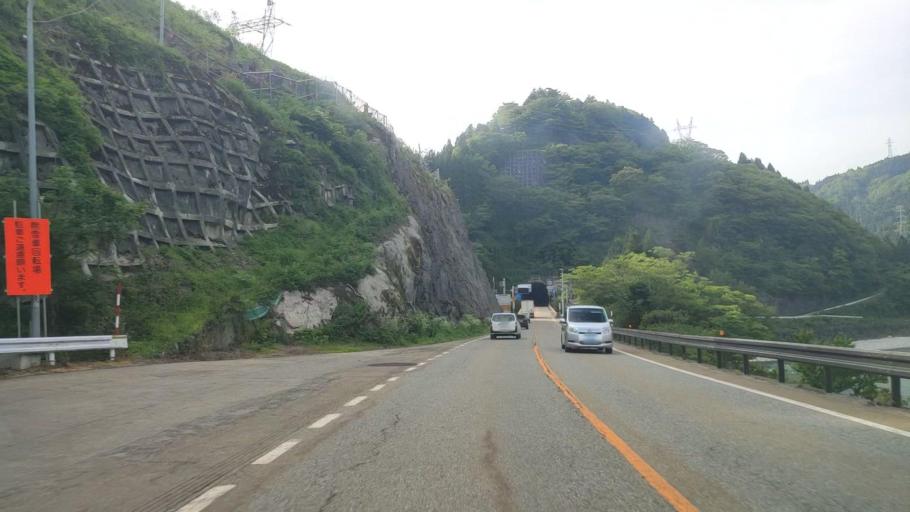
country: JP
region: Toyama
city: Yatsuomachi-higashikumisaka
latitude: 36.4601
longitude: 137.2483
